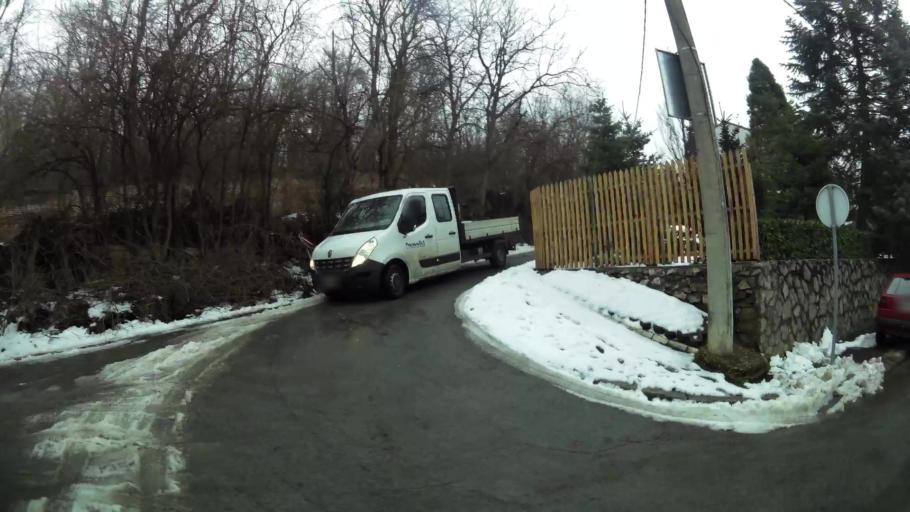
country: RS
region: Central Serbia
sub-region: Belgrade
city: Rakovica
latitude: 44.7585
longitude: 20.4496
